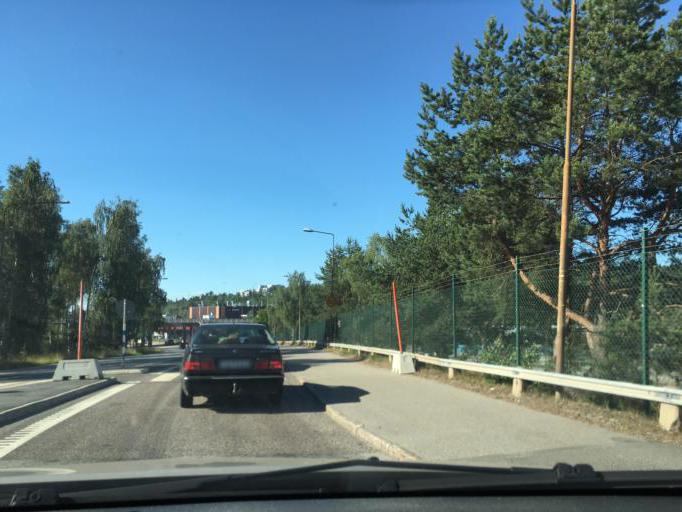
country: SE
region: Stockholm
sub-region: Sodertalje Kommun
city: Soedertaelje
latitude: 59.1786
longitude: 17.6396
